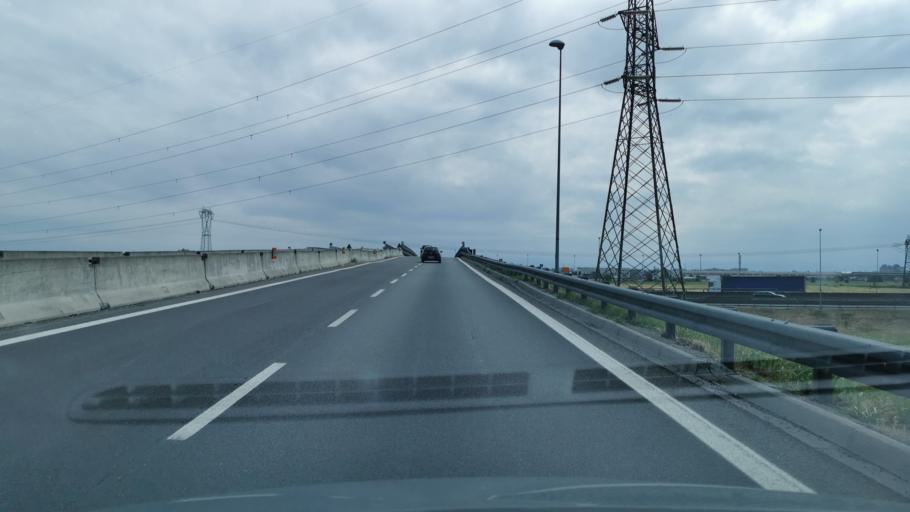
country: IT
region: Emilia-Romagna
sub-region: Provincia di Piacenza
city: Piacenza
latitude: 45.0587
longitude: 9.7433
